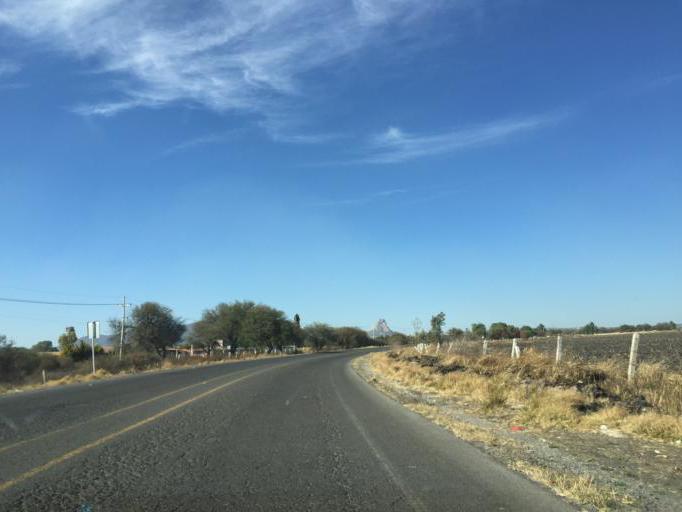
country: MX
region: Queretaro
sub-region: Colon
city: Los Benitos
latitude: 20.6656
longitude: -99.9373
